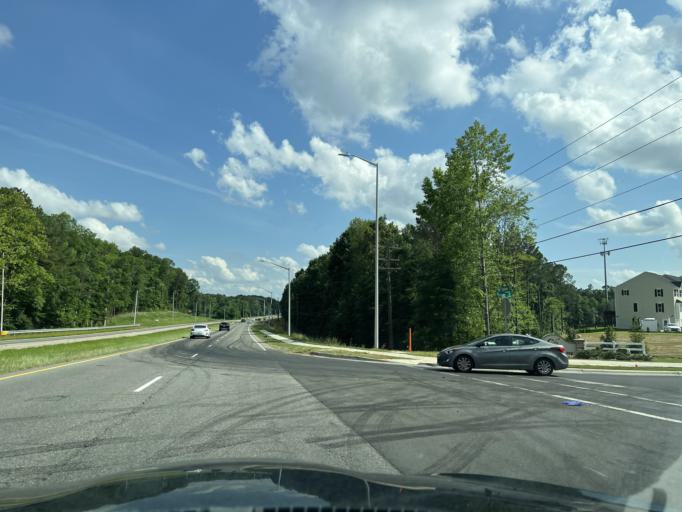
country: US
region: North Carolina
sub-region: Durham County
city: Durham
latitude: 35.9494
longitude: -78.8891
